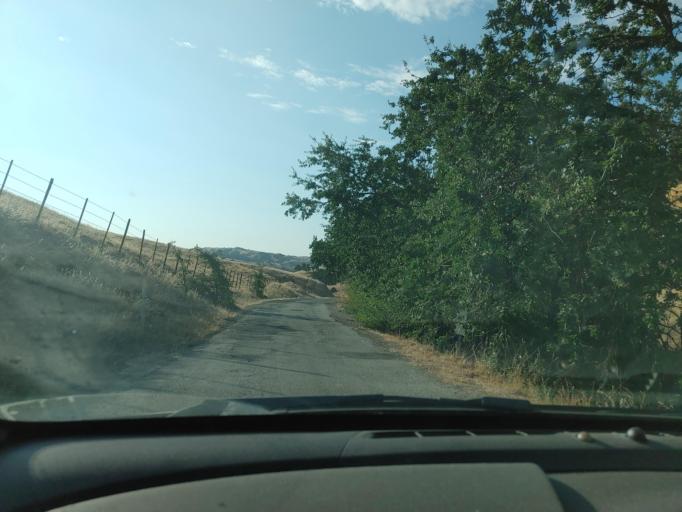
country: US
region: California
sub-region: San Benito County
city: Ridgemark
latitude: 36.7569
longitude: -121.1679
